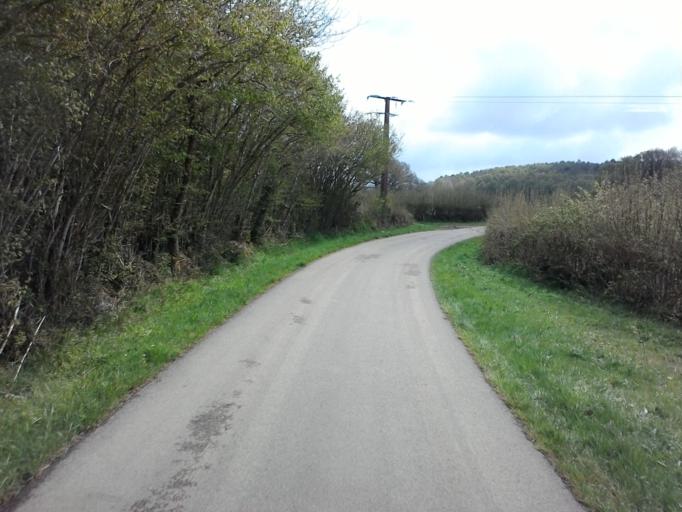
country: FR
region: Bourgogne
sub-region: Departement de la Cote-d'Or
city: Saulieu
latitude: 47.2429
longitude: 4.2039
